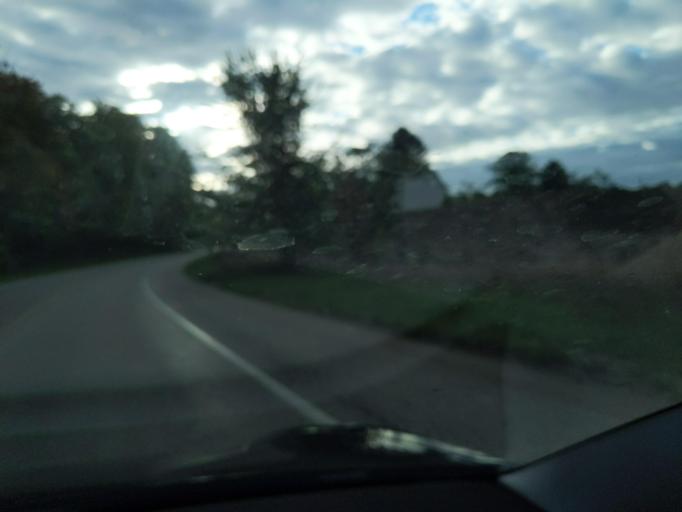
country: US
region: Michigan
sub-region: Kalkaska County
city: Rapid City
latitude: 44.7805
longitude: -85.2892
